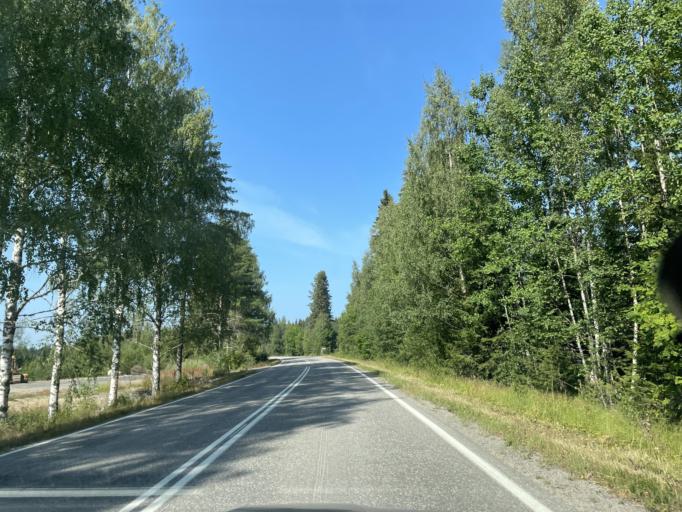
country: FI
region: Central Finland
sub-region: Saarijaervi-Viitasaari
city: Pihtipudas
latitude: 63.3739
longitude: 25.6109
